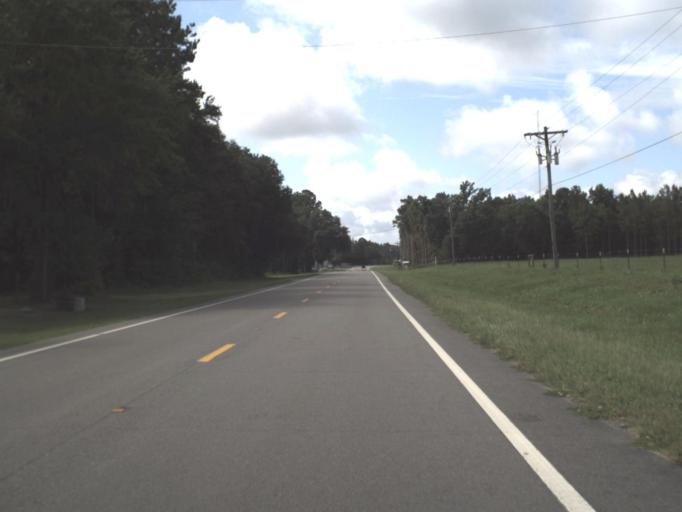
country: US
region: Florida
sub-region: Columbia County
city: Five Points
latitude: 30.3639
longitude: -82.6196
